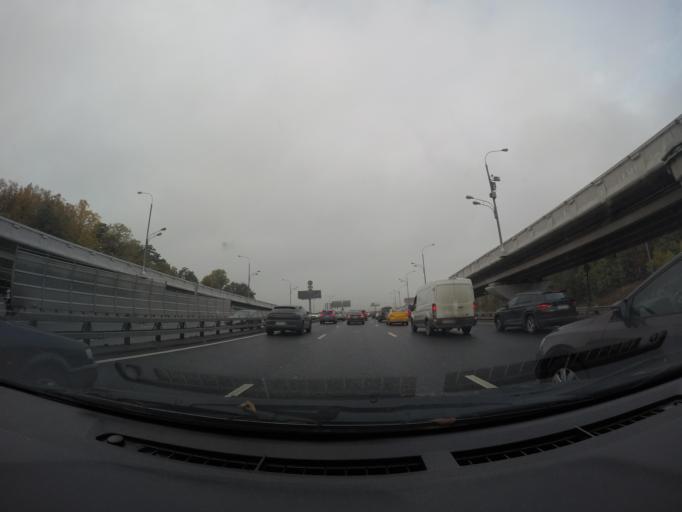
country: RU
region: Moscow
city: Rublevo
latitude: 55.7920
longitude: 37.3616
